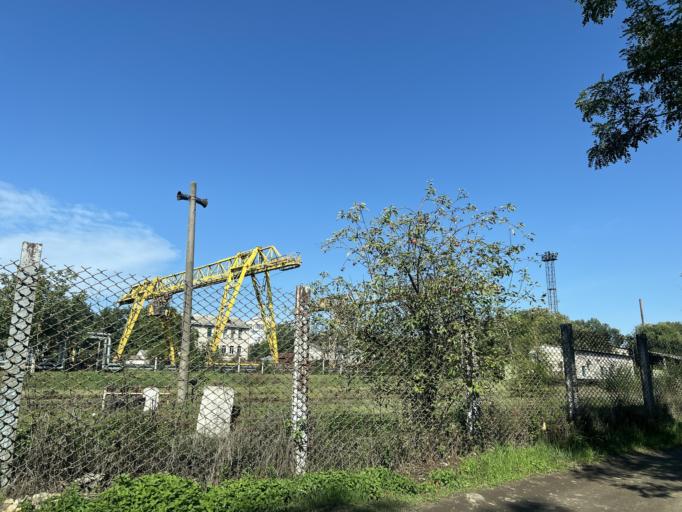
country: MD
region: Ungheni
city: Ungheni
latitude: 47.2032
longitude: 27.8017
